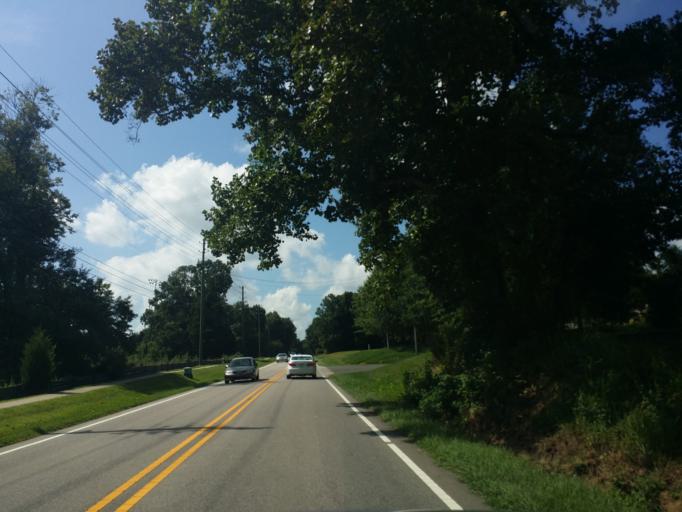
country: US
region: North Carolina
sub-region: Wake County
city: West Raleigh
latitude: 35.8900
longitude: -78.7128
